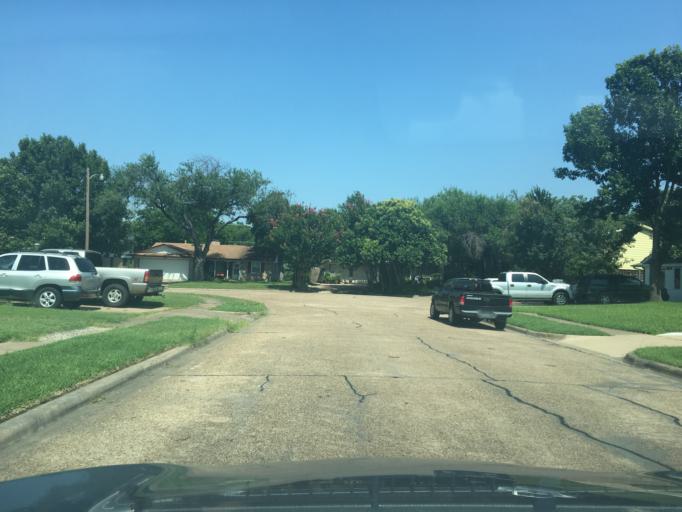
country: US
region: Texas
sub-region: Dallas County
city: Richardson
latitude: 32.9258
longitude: -96.7014
